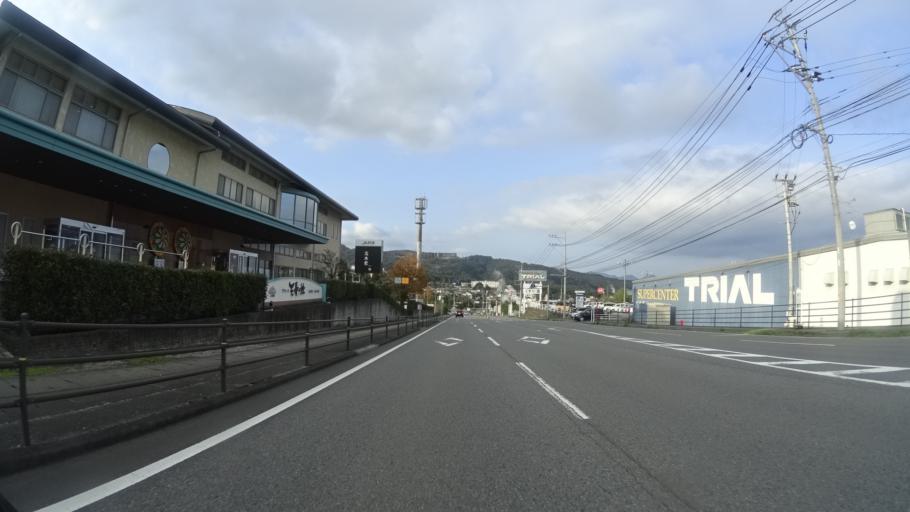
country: JP
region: Oita
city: Beppu
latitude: 33.3033
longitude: 131.4614
